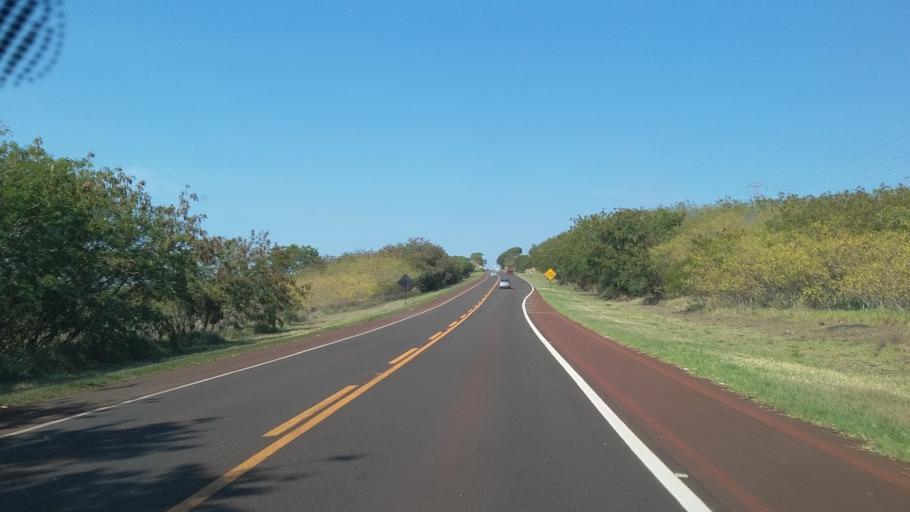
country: BR
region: Parana
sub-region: Bandeirantes
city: Bandeirantes
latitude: -23.1181
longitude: -50.3461
